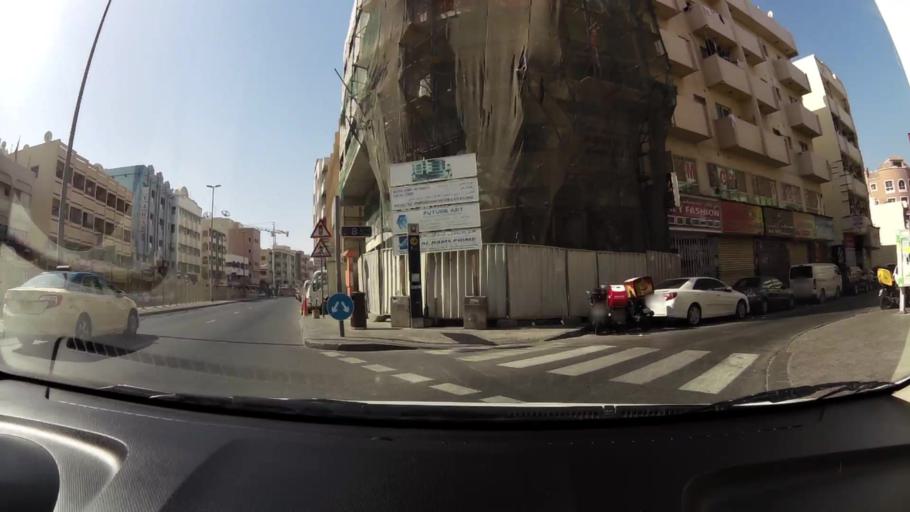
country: AE
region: Ash Shariqah
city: Sharjah
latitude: 25.2759
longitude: 55.3055
